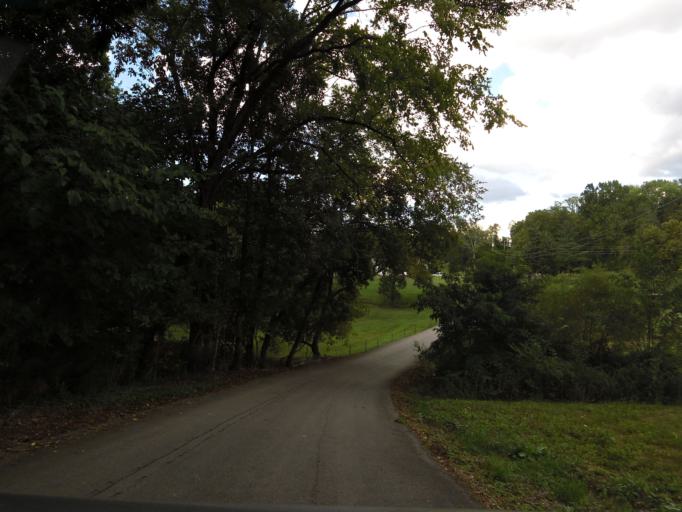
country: US
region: Tennessee
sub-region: Knox County
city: Mascot
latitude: 36.1153
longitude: -83.7780
